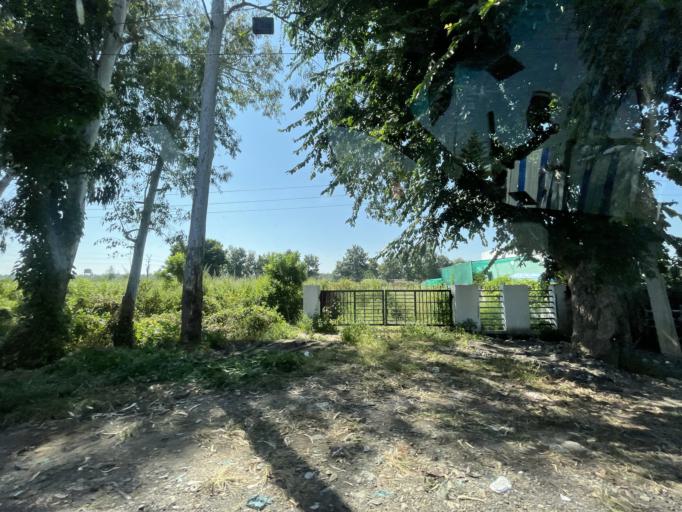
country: IN
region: Uttarakhand
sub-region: Naini Tal
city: Haldwani
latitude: 29.2124
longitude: 79.4583
